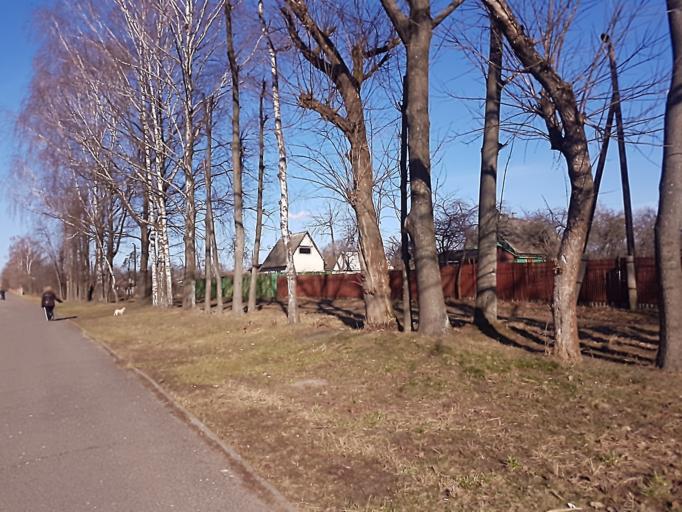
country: BY
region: Mogilev
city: Babruysk
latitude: 53.1849
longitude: 29.2234
